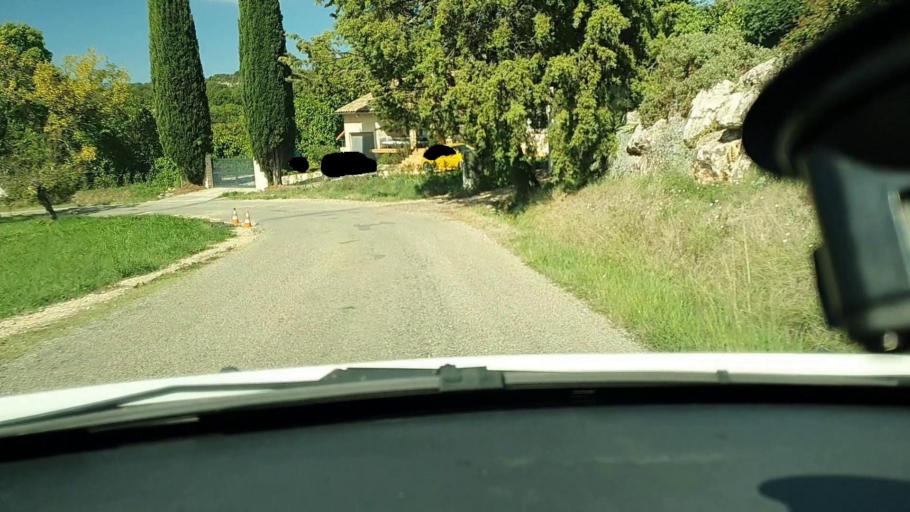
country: FR
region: Languedoc-Roussillon
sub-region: Departement du Gard
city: Goudargues
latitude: 44.1706
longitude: 4.3876
